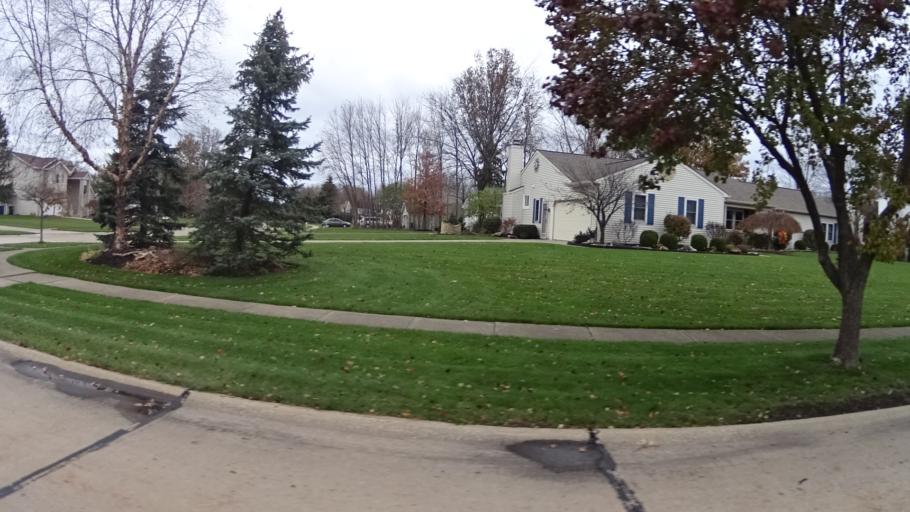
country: US
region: Ohio
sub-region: Lorain County
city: Avon Center
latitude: 41.4871
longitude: -81.9912
